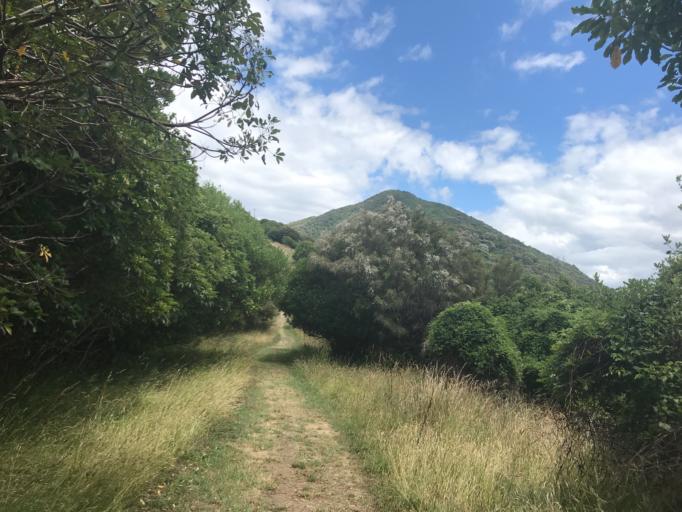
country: NZ
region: Marlborough
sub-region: Marlborough District
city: Picton
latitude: -41.2124
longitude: 173.9975
